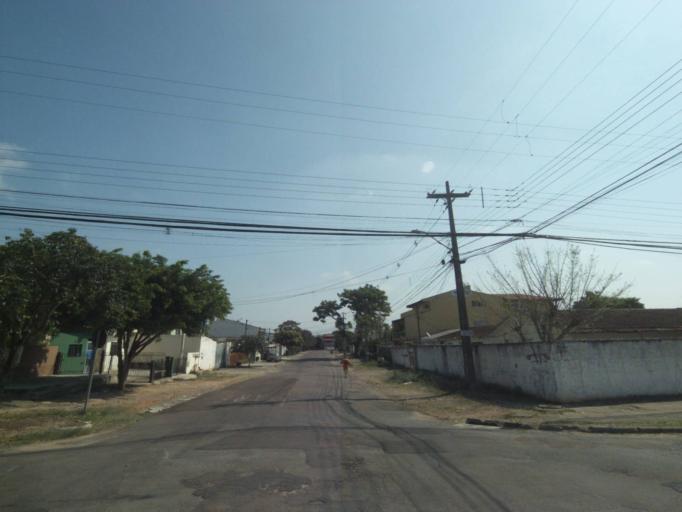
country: BR
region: Parana
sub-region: Curitiba
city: Curitiba
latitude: -25.4838
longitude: -49.3310
